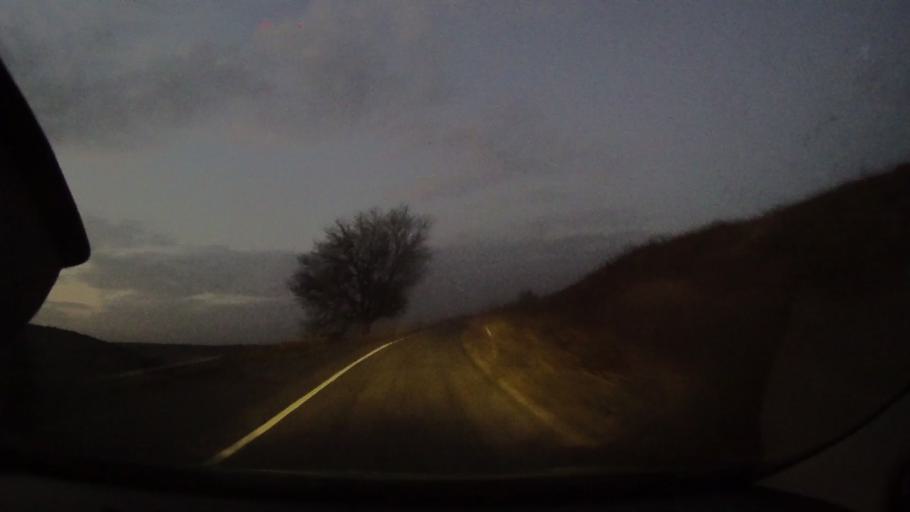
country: RO
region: Constanta
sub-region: Comuna Aliman
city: Aliman
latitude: 44.1488
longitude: 27.8331
